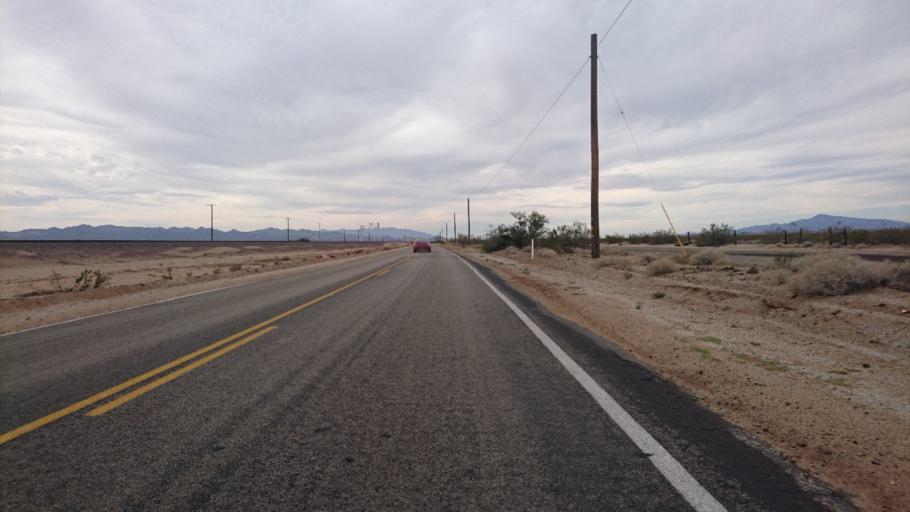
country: US
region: California
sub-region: San Bernardino County
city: Needles
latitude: 34.8975
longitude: -115.0933
